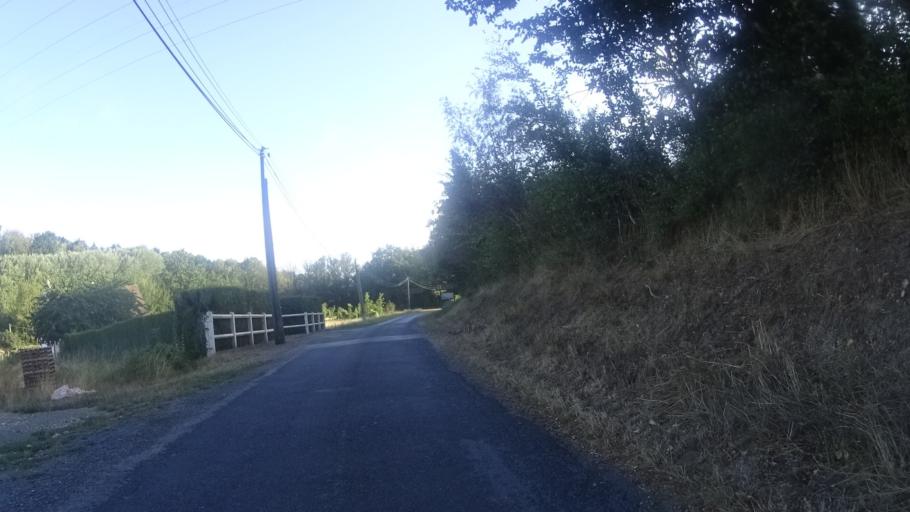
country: FR
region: Picardie
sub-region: Departement de l'Oise
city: Verberie
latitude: 49.3040
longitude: 2.6941
